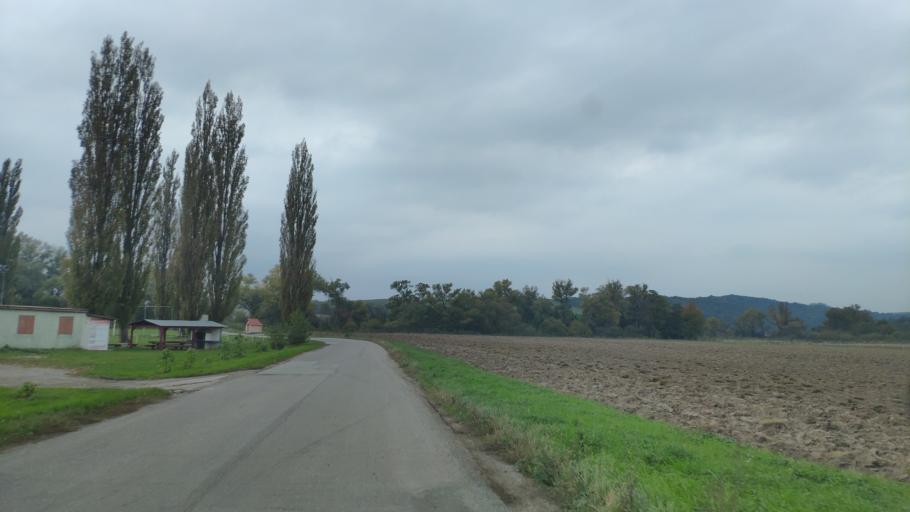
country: SK
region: Kosicky
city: Kosice
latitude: 48.6376
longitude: 21.3786
